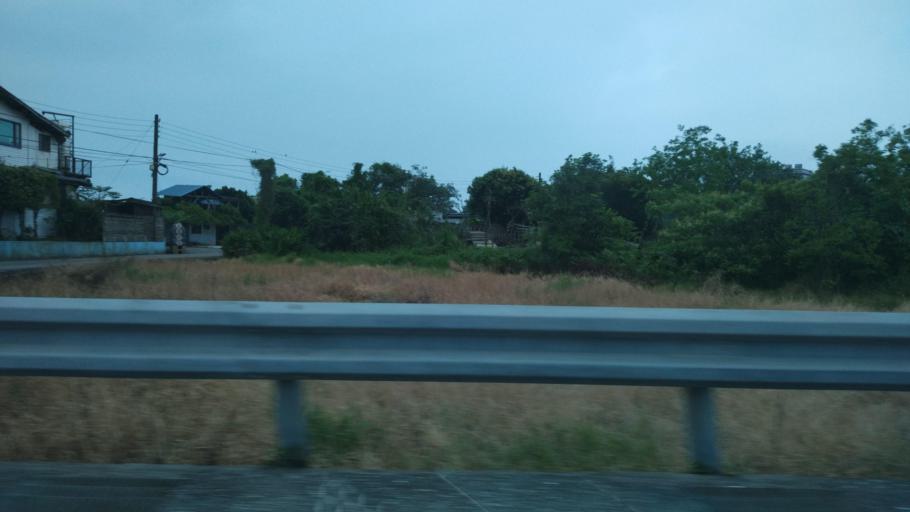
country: TW
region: Taiwan
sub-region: Keelung
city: Keelung
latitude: 25.2110
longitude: 121.6485
